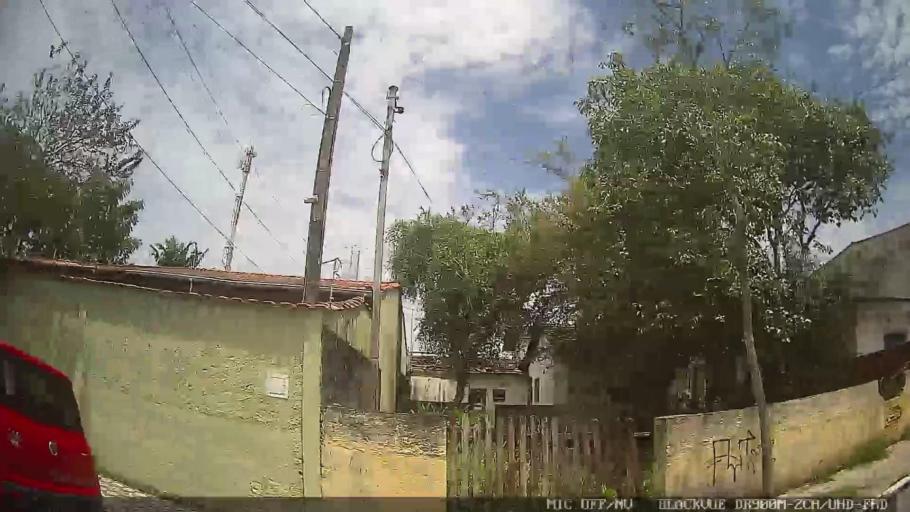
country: BR
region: Sao Paulo
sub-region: Ribeirao Pires
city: Ribeirao Pires
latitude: -23.7131
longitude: -46.4222
